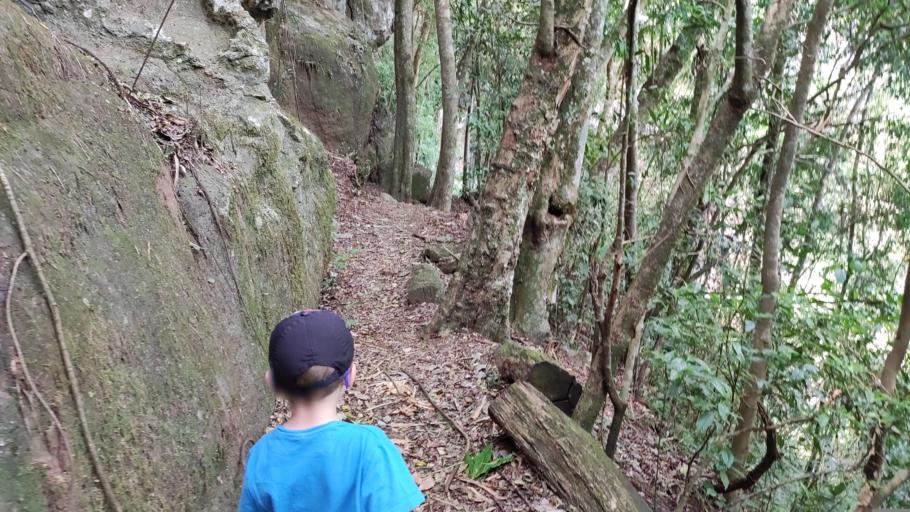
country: AR
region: Misiones
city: Dos de Mayo
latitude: -26.9981
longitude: -54.6251
